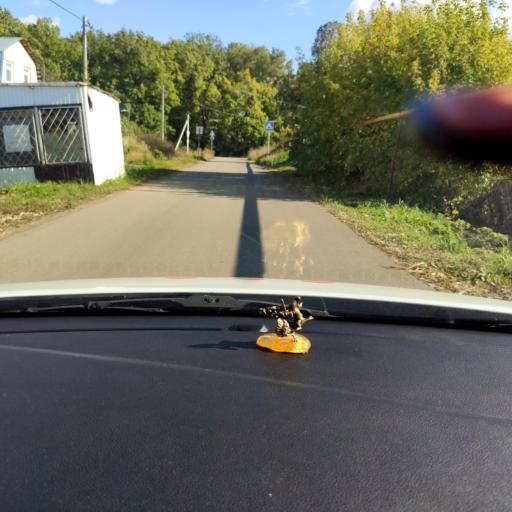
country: RU
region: Tatarstan
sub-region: Gorod Kazan'
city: Kazan
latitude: 55.6995
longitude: 49.0907
